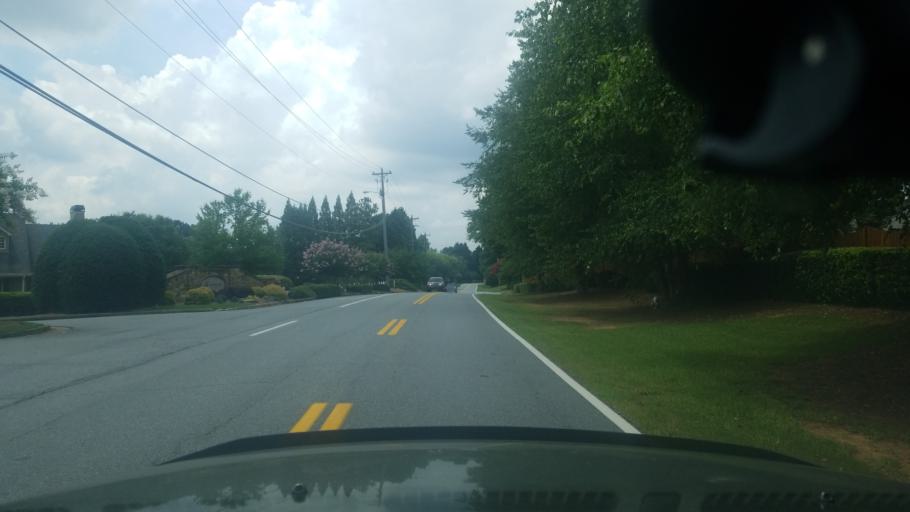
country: US
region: Georgia
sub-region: Fulton County
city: Johns Creek
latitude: 34.0980
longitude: -84.1922
